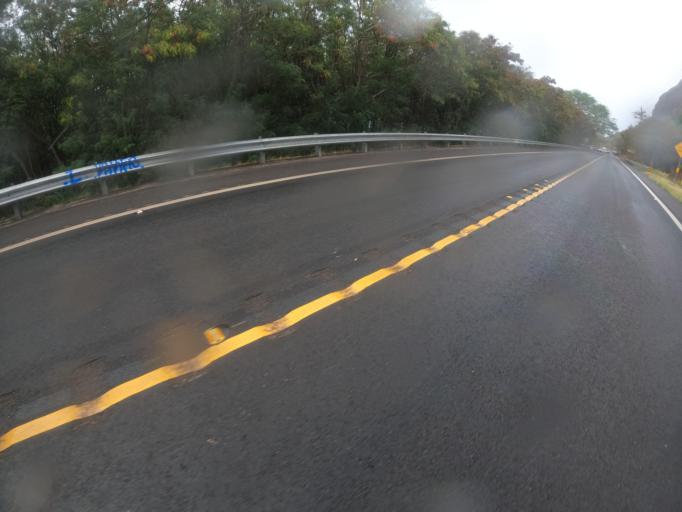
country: US
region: Hawaii
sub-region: Honolulu County
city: Makaha Valley
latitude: 21.5365
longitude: -158.2300
